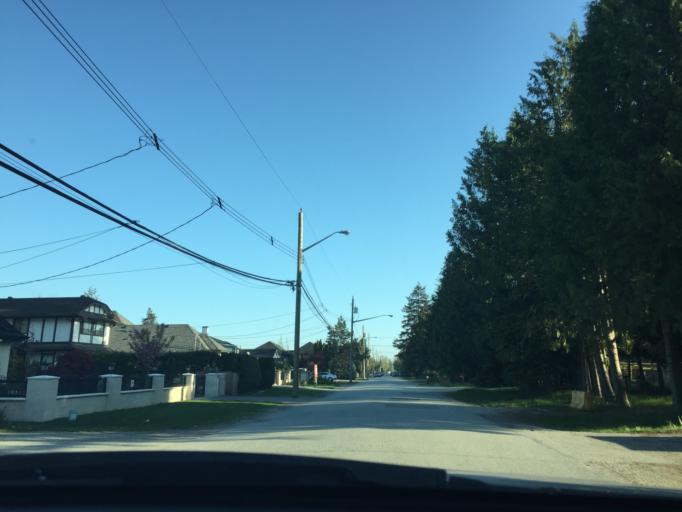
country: CA
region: British Columbia
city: Richmond
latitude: 49.1586
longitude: -123.1198
